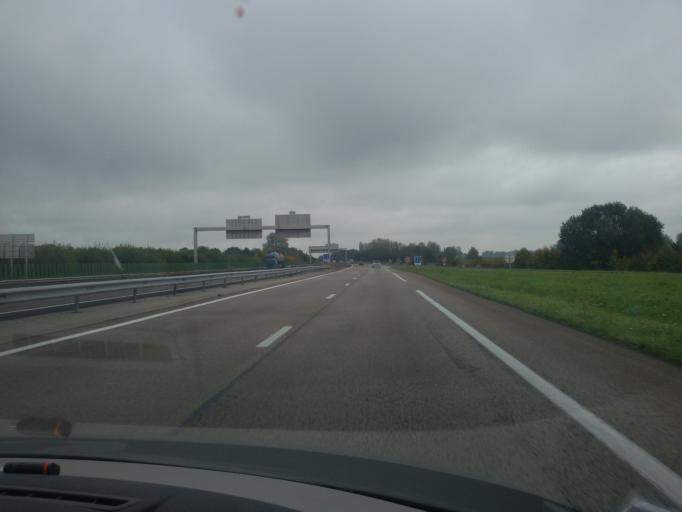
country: FR
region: Haute-Normandie
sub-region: Departement de l'Eure
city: Corneville-sur-Risle
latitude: 49.3803
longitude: 0.6119
